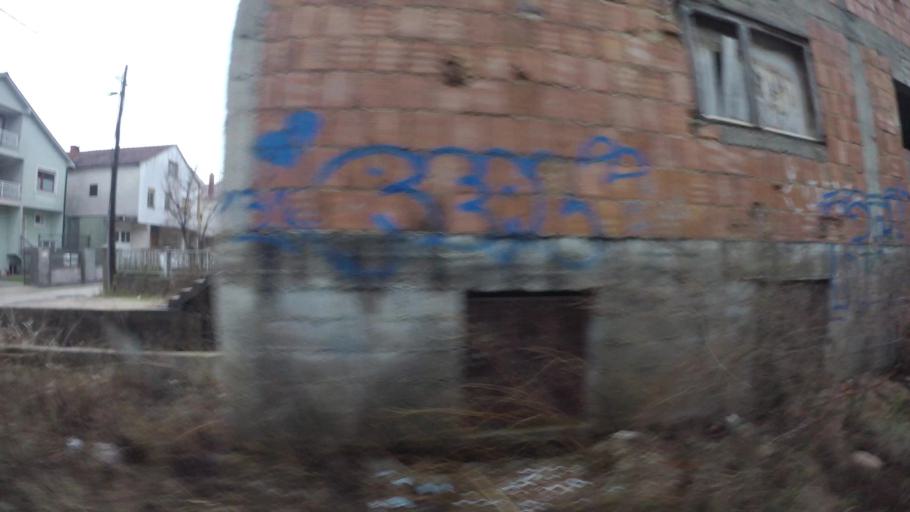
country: BA
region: Federation of Bosnia and Herzegovina
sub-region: Hercegovacko-Bosanski Kanton
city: Mostar
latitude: 43.3559
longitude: 17.8021
